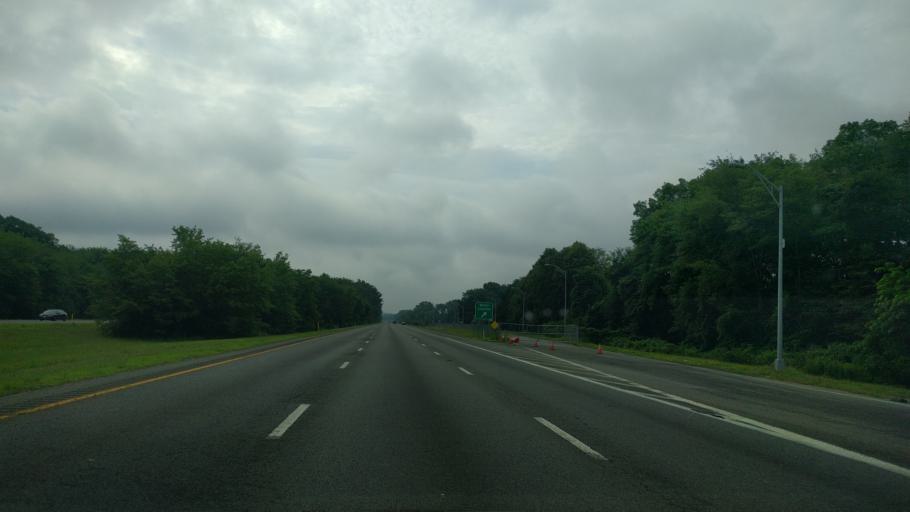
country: US
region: Massachusetts
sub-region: Bristol County
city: Seekonk
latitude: 41.7906
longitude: -71.3066
